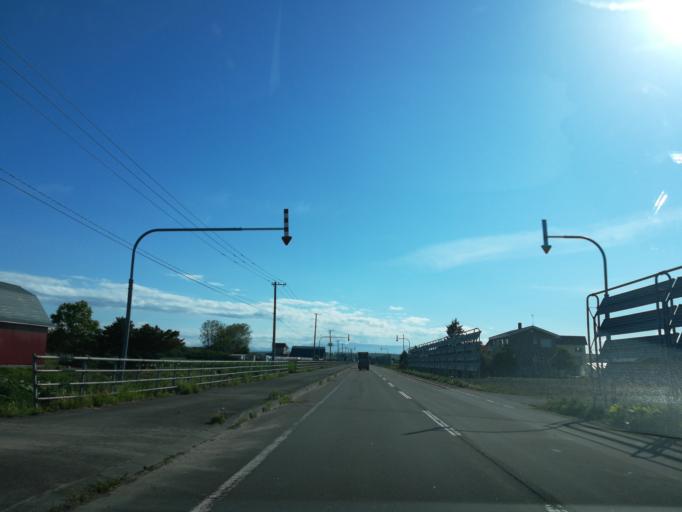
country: JP
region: Hokkaido
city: Kitahiroshima
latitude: 43.0449
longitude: 141.5927
